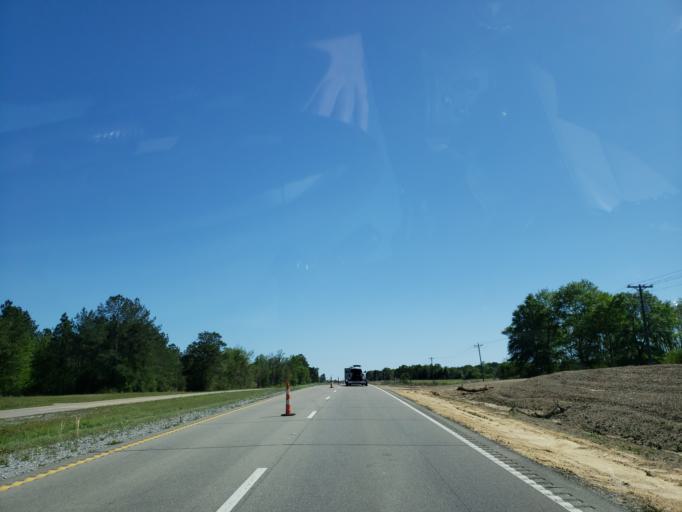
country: US
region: Mississippi
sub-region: Lamar County
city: Purvis
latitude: 31.0794
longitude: -89.2112
